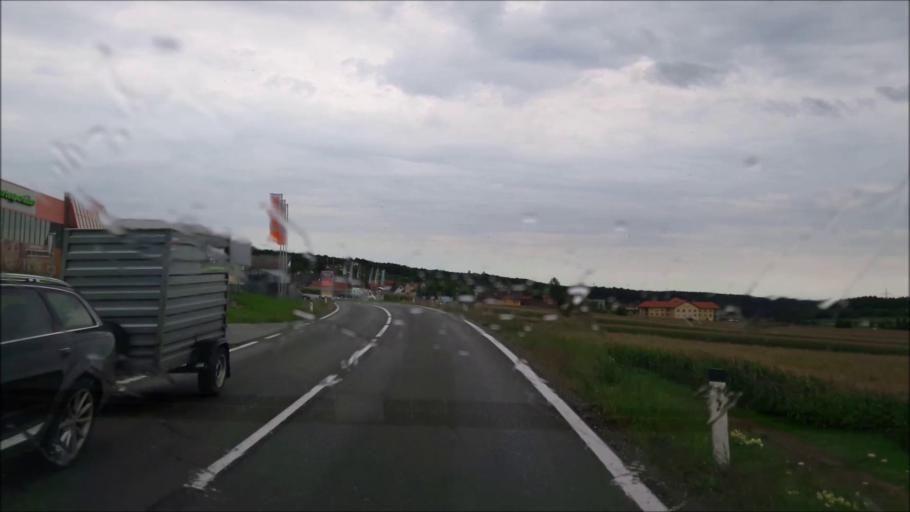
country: AT
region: Styria
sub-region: Politischer Bezirk Hartberg-Fuerstenfeld
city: Sankt Johann in der Haide
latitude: 47.2809
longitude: 16.0164
